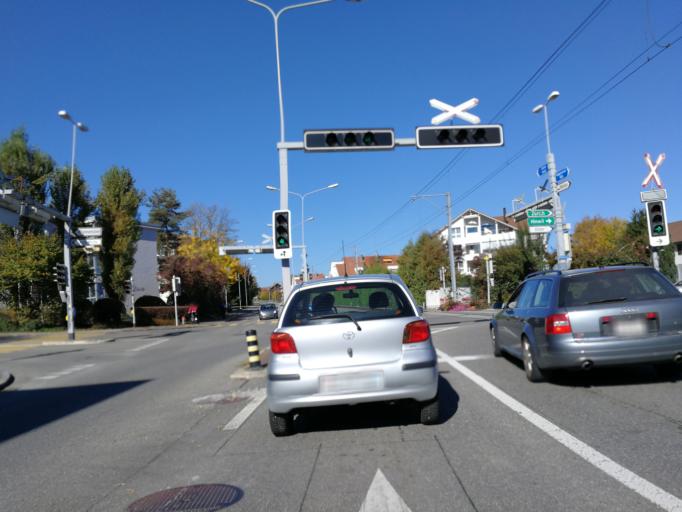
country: CH
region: Zurich
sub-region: Bezirk Uster
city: Egg
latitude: 47.3027
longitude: 8.6886
